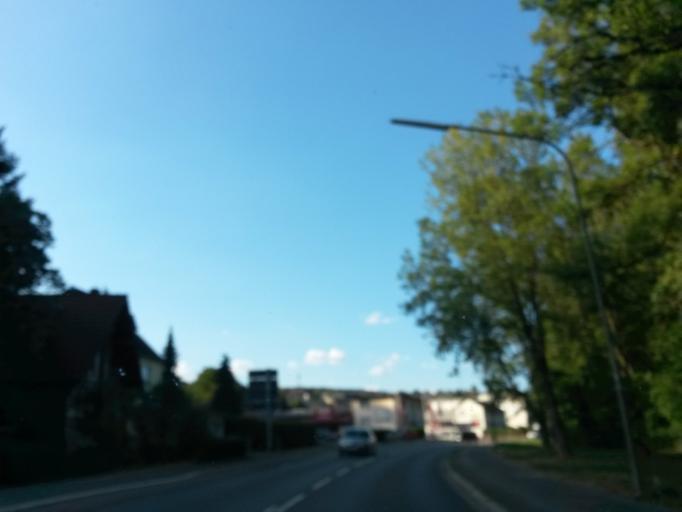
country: DE
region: North Rhine-Westphalia
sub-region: Regierungsbezirk Koln
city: Gummersbach
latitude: 51.0198
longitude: 7.5726
